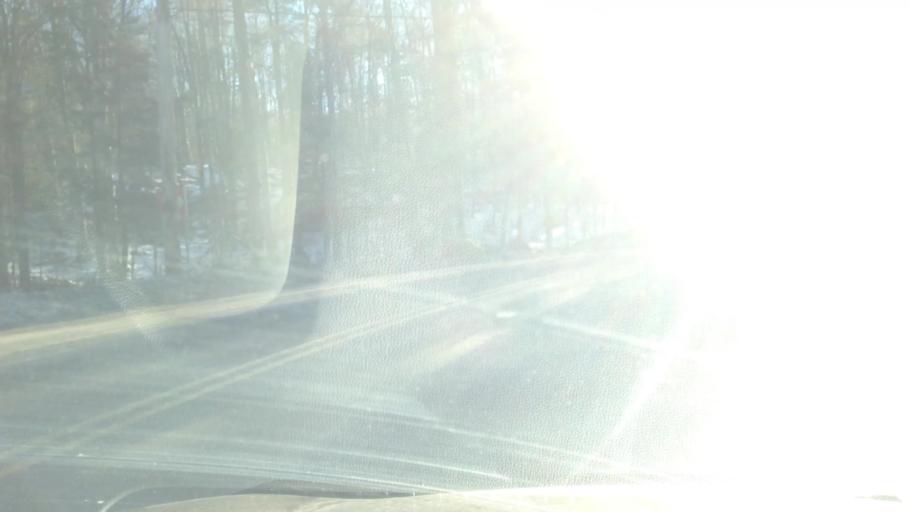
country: CA
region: Quebec
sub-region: Laurentides
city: Mont-Tremblant
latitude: 46.0266
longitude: -74.6041
